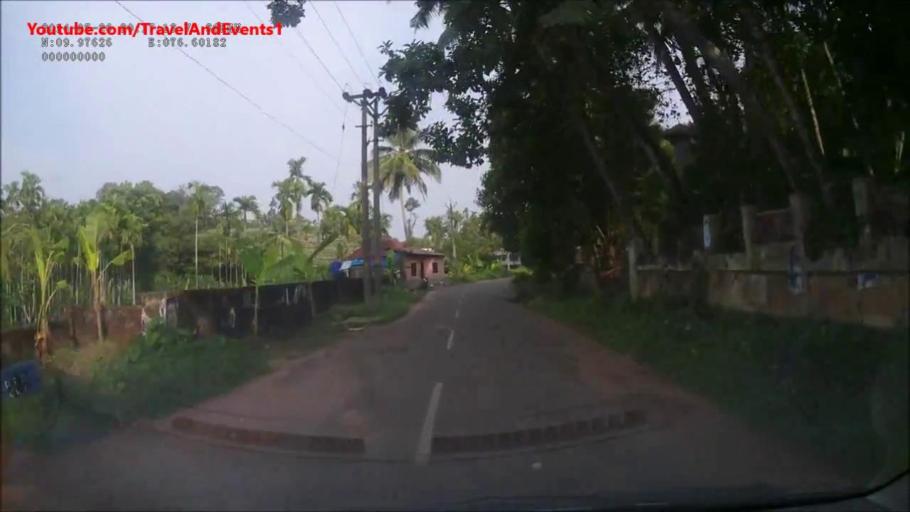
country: IN
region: Kerala
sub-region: Ernakulam
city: Muvattupula
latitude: 9.9707
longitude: 76.6079
